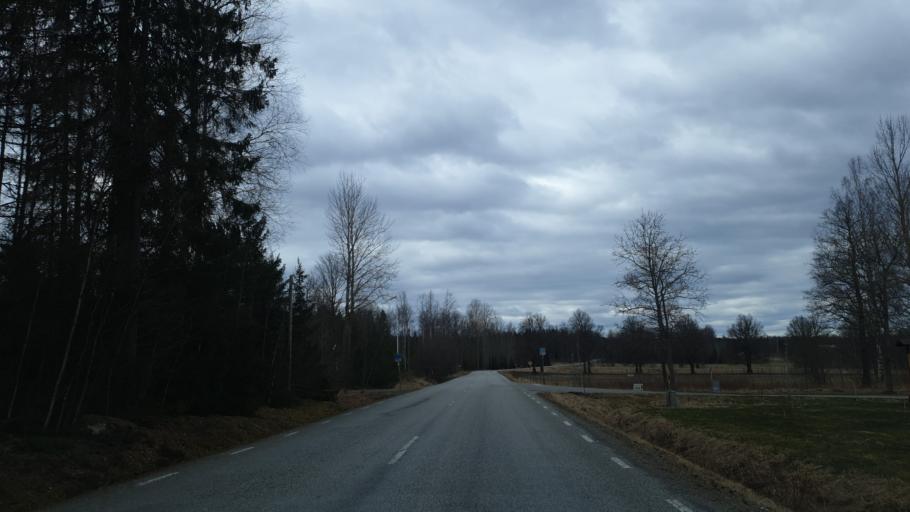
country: SE
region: OErebro
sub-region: Nora Kommun
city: As
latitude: 59.5815
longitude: 14.9718
